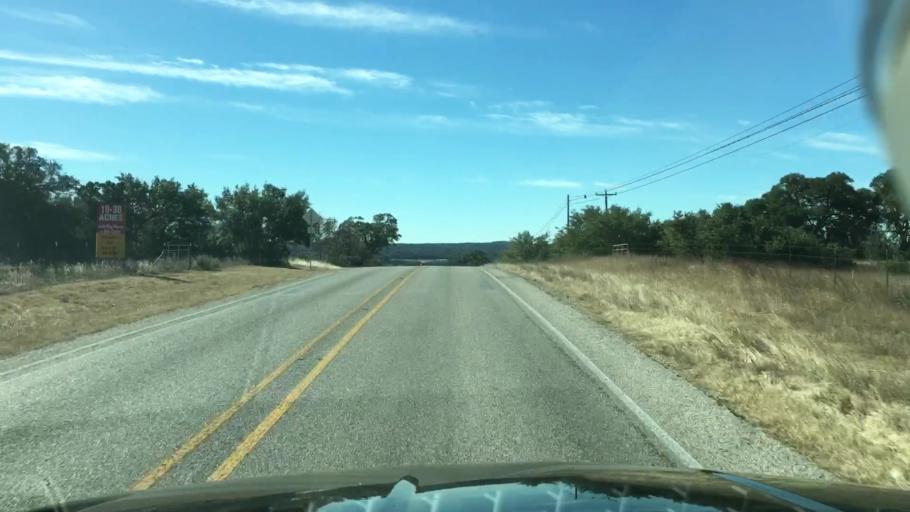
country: US
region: Texas
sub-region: Blanco County
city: Blanco
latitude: 30.1097
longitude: -98.3444
